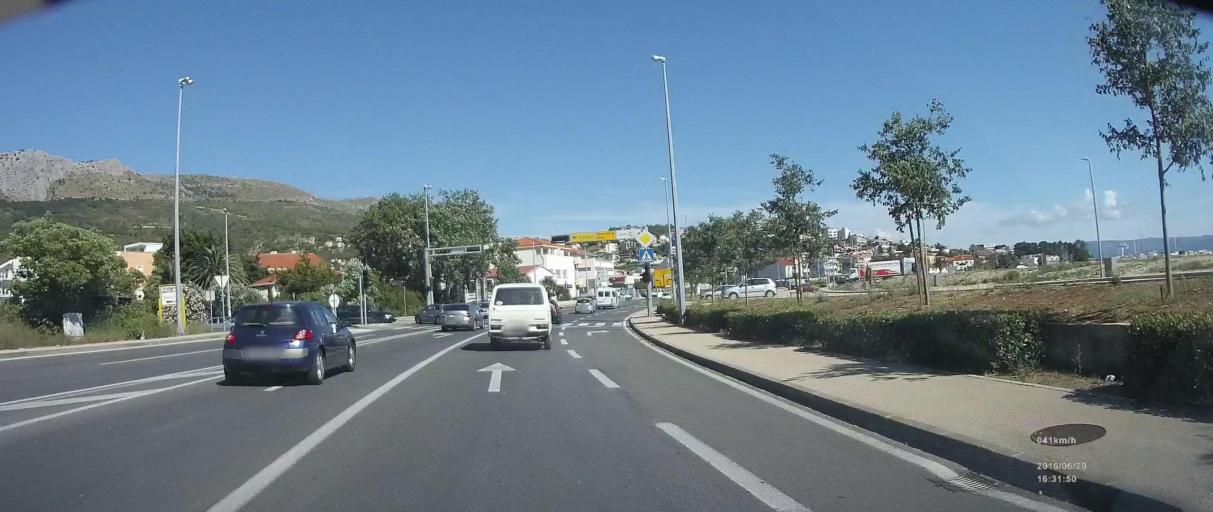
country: HR
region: Splitsko-Dalmatinska
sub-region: Grad Split
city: Stobrec
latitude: 43.5041
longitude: 16.5327
